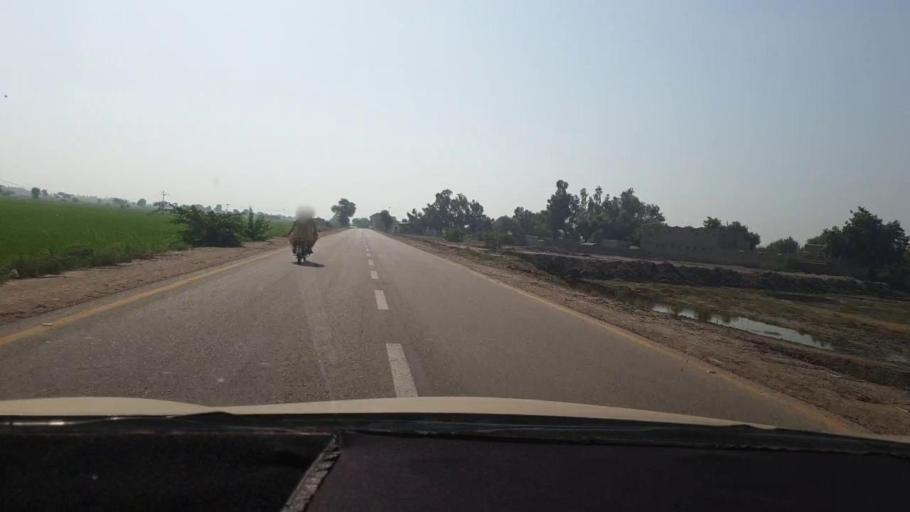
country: PK
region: Sindh
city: Miro Khan
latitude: 27.7238
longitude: 68.1394
